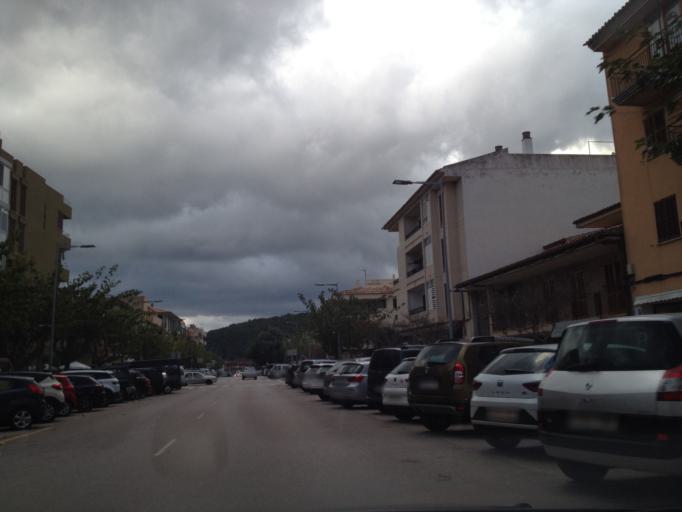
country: ES
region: Balearic Islands
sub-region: Illes Balears
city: Pollenca
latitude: 39.8755
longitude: 3.0191
